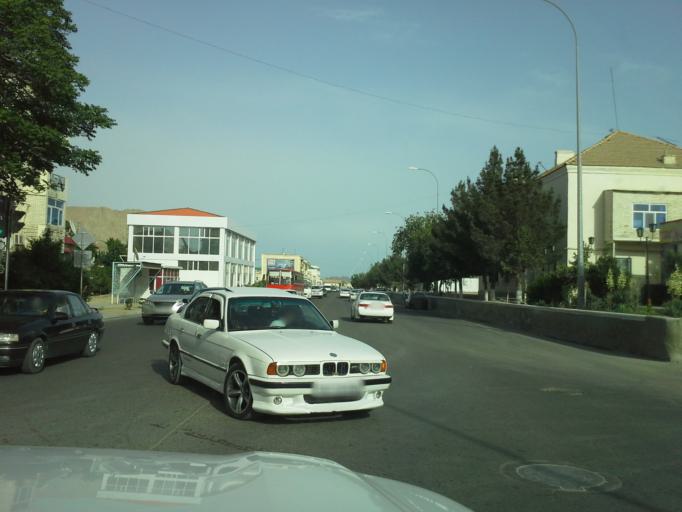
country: TM
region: Balkan
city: Turkmenbasy
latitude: 40.0154
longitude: 52.9808
